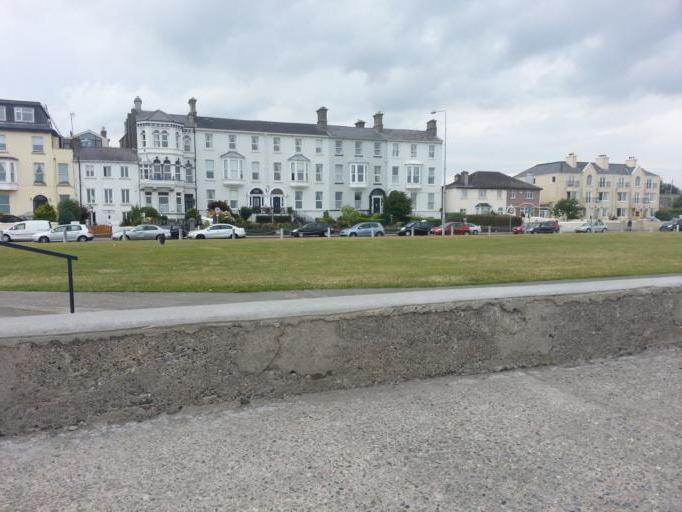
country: IE
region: Leinster
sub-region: Wicklow
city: Bray
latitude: 53.1999
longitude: -6.0956
